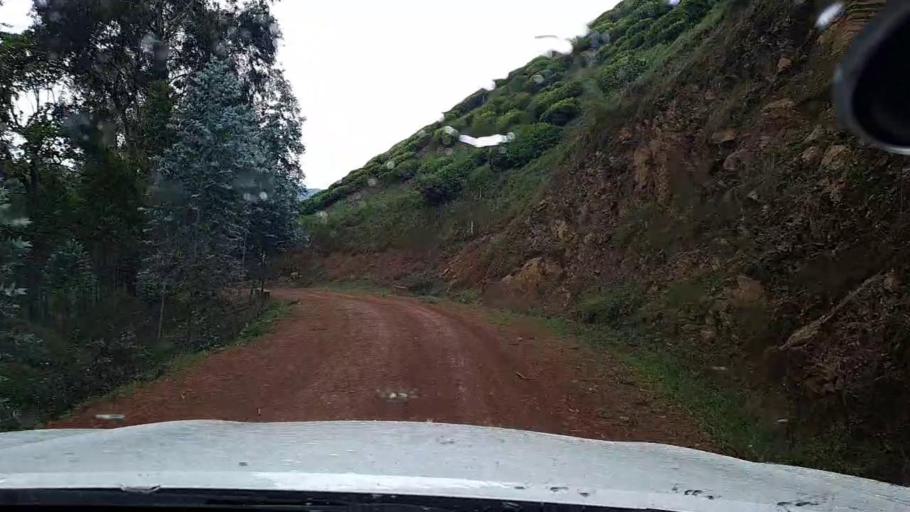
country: RW
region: Western Province
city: Kibuye
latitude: -2.1652
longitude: 29.4353
